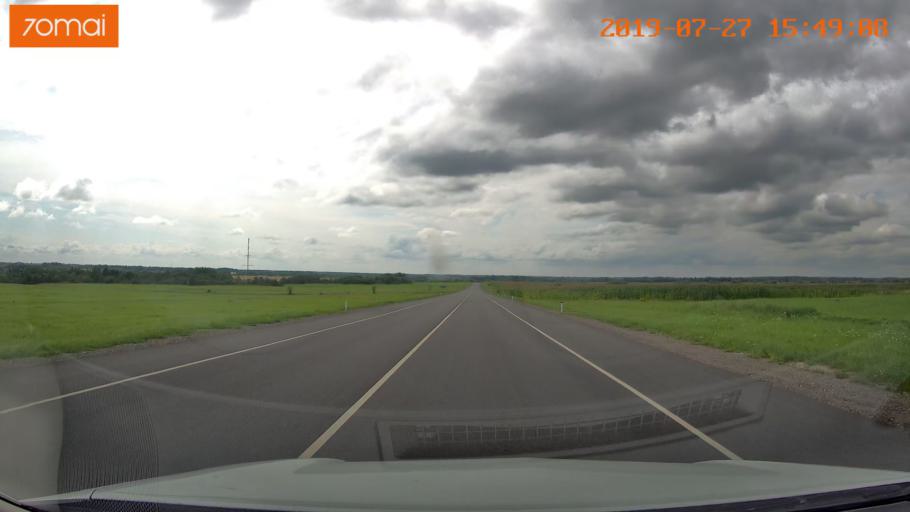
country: RU
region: Kaliningrad
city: Gusev
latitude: 54.6016
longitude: 22.0428
